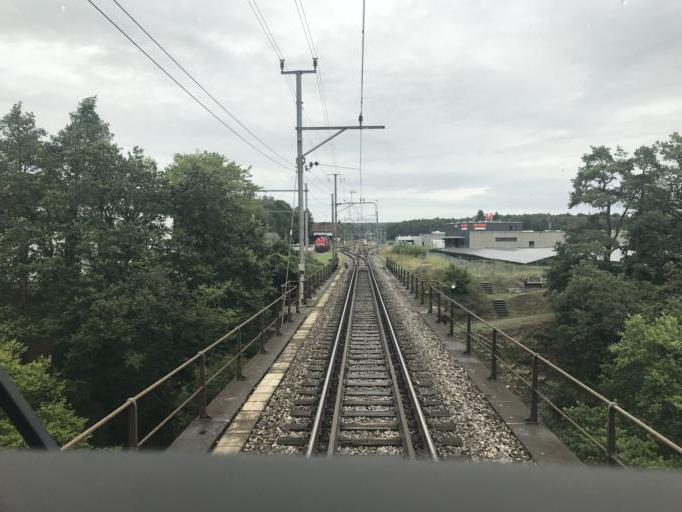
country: CH
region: Zurich
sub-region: Bezirk Buelach
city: Seglingen
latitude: 47.5788
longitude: 8.5118
